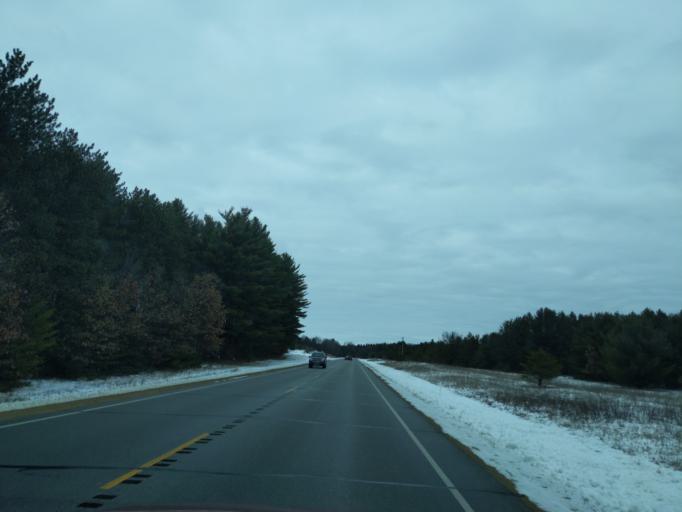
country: US
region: Wisconsin
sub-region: Waushara County
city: Wautoma
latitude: 43.9504
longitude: -89.3175
